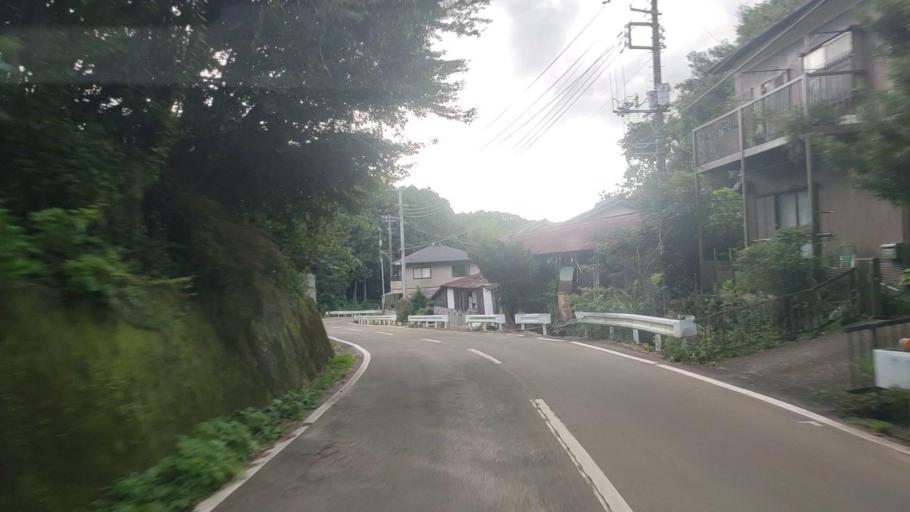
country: JP
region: Shizuoka
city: Mishima
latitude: 35.1369
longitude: 138.9763
